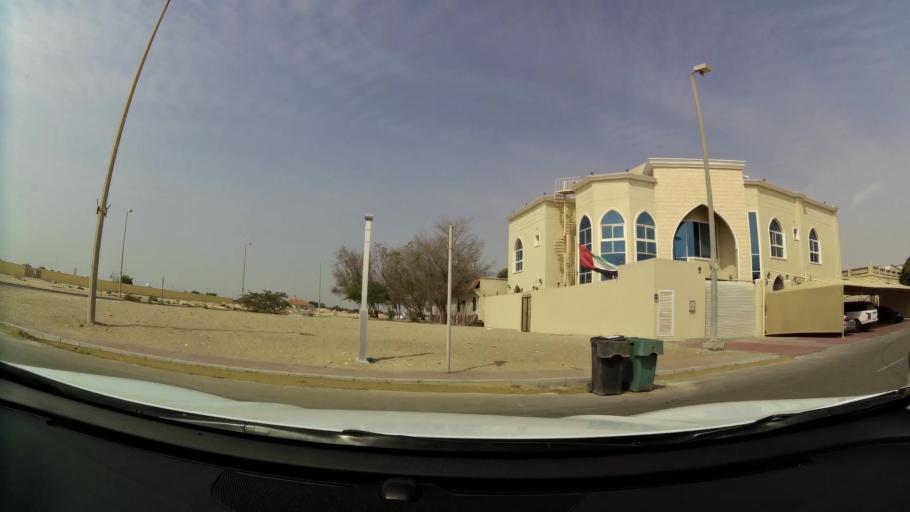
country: AE
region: Abu Dhabi
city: Abu Dhabi
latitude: 24.5493
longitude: 54.6777
